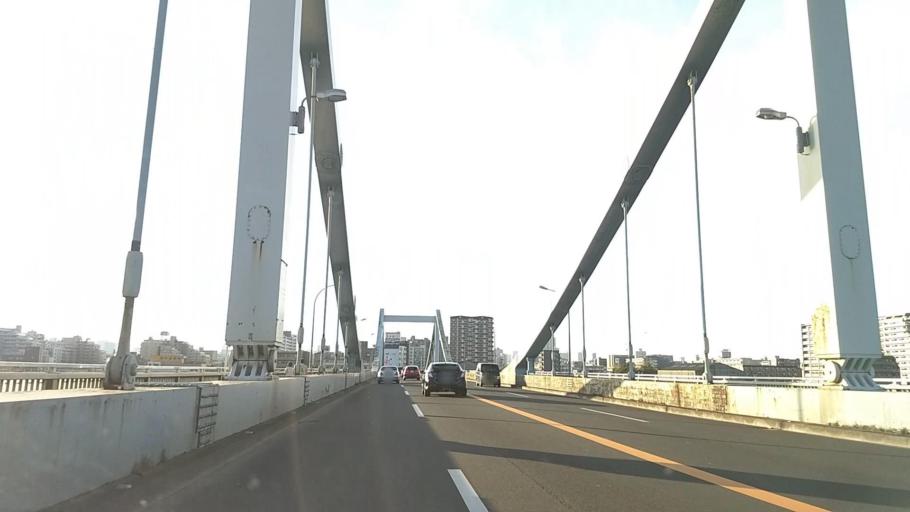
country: JP
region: Tokyo
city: Urayasu
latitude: 35.6713
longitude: 139.8458
